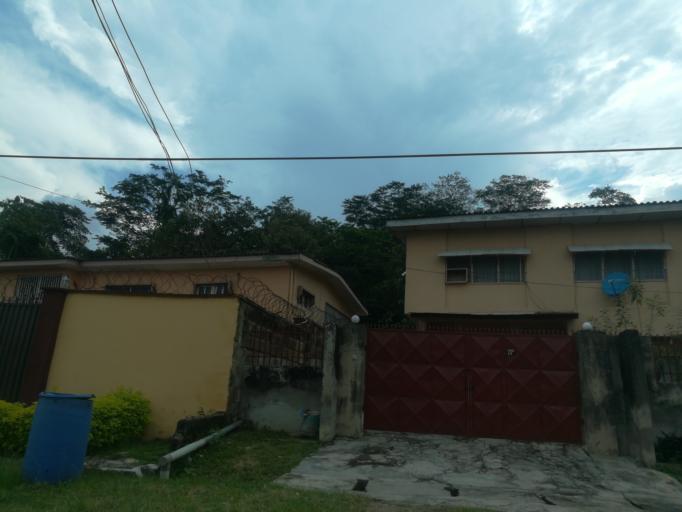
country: NG
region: Oyo
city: Ibadan
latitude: 7.4132
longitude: 3.8995
